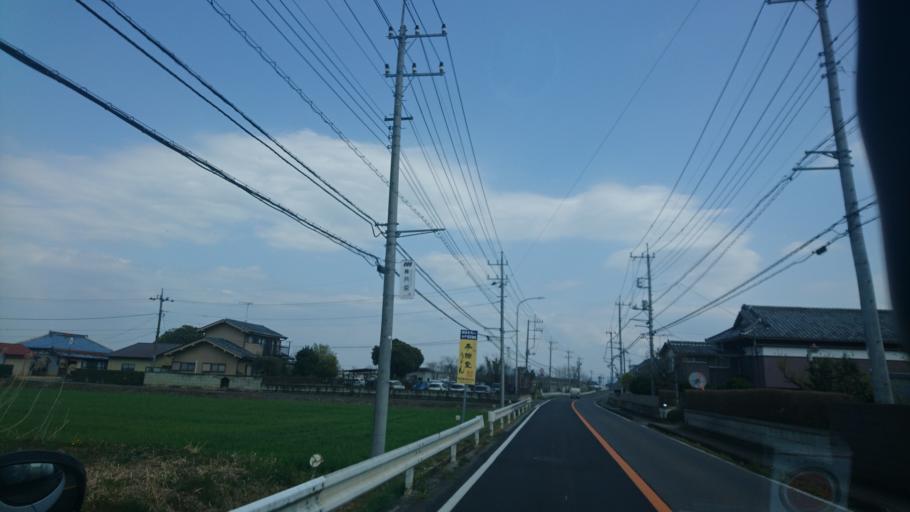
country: JP
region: Ibaraki
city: Yuki
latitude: 36.2953
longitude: 139.8943
